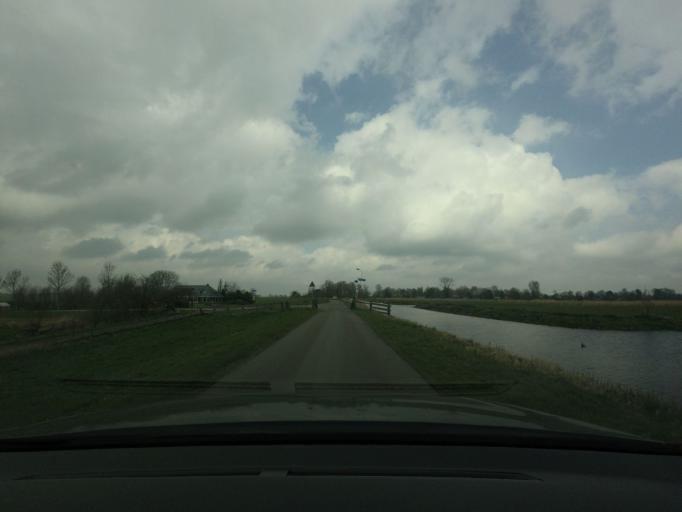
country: NL
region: Utrecht
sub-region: Gemeente De Ronde Venen
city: Mijdrecht
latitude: 52.1886
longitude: 4.8203
